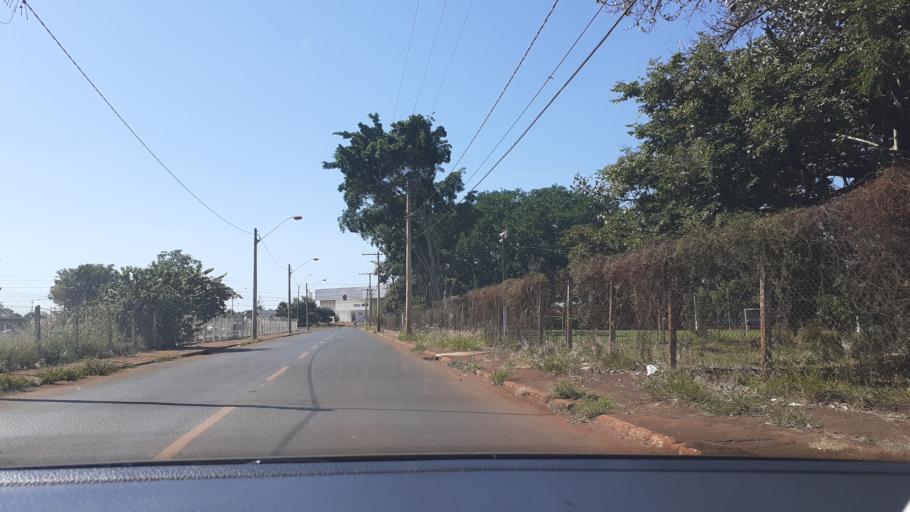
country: BR
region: Goias
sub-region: Itumbiara
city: Itumbiara
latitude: -18.4116
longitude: -49.2500
